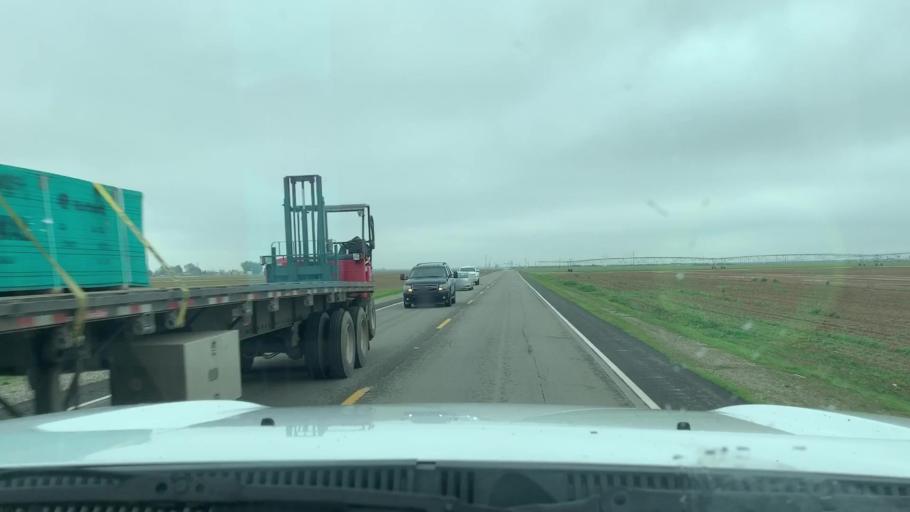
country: US
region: California
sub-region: Kern County
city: Rosedale
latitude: 35.4512
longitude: -119.1541
